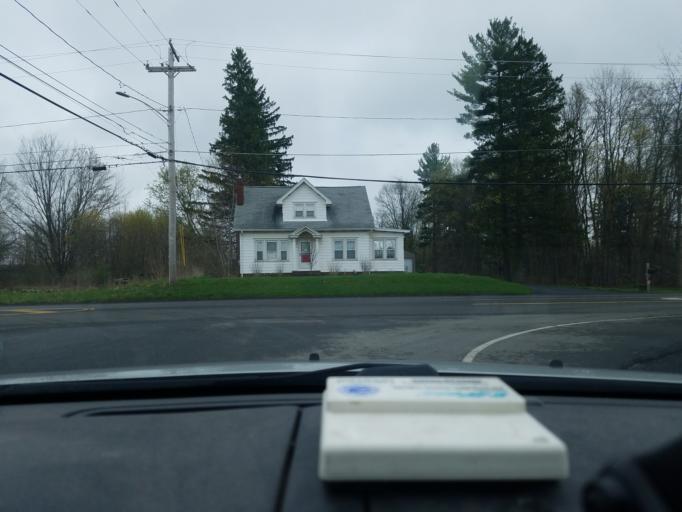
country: US
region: New York
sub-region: Onondaga County
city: North Syracuse
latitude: 43.1626
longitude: -76.0928
